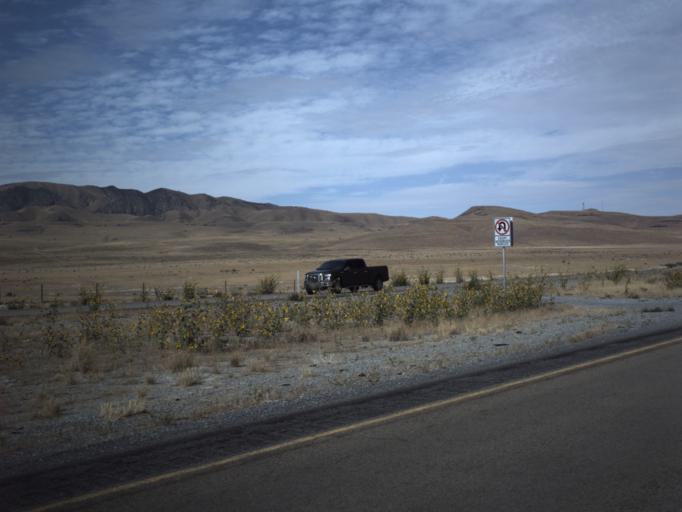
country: US
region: Utah
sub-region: Tooele County
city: Grantsville
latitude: 40.7886
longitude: -112.8282
